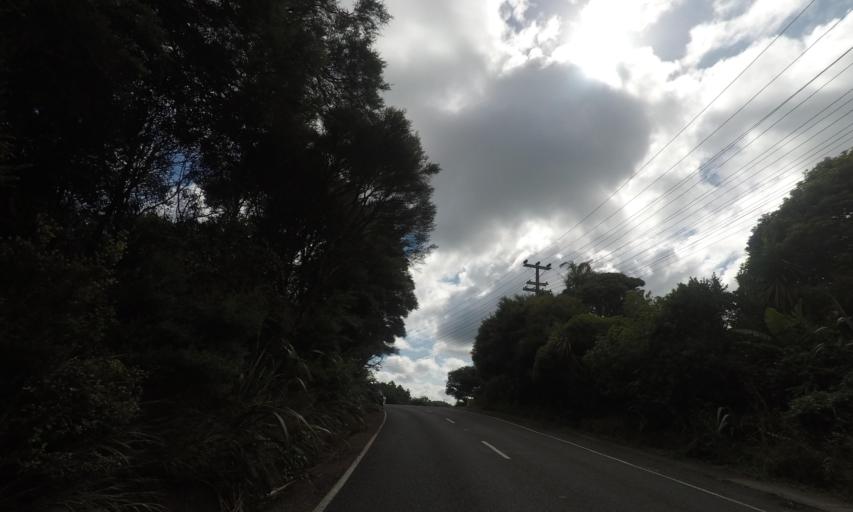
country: NZ
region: Auckland
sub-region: Auckland
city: Titirangi
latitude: -36.9567
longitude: 174.6248
